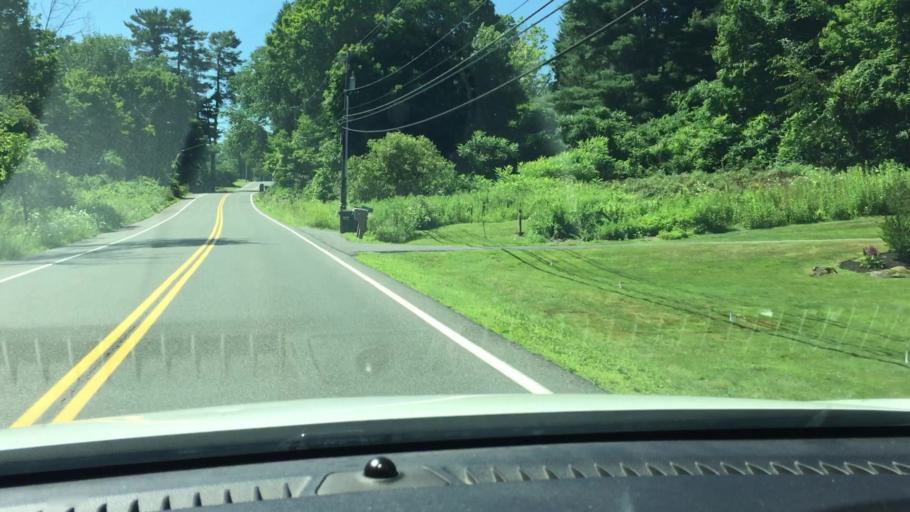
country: US
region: Massachusetts
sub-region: Berkshire County
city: Lenox
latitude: 42.3636
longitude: -73.2596
